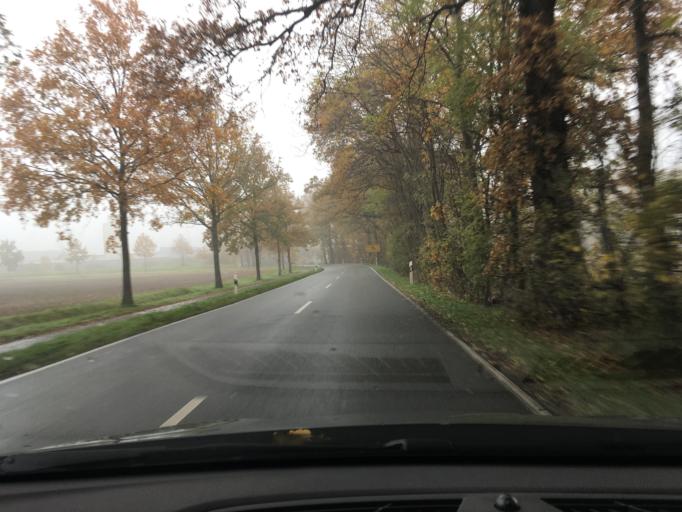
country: DE
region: North Rhine-Westphalia
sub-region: Regierungsbezirk Munster
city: Ahaus
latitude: 52.1188
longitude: 6.9205
